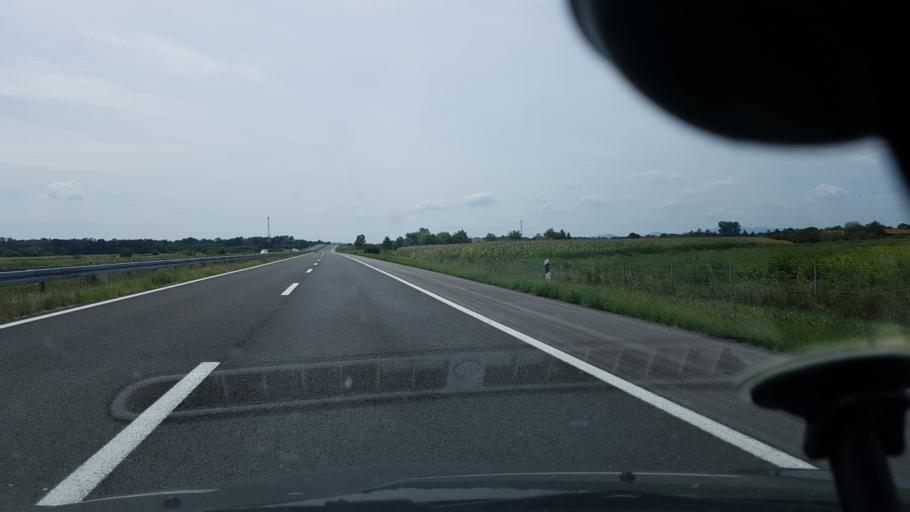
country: HR
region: Medimurska
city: Palovec
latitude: 46.3851
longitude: 16.5572
